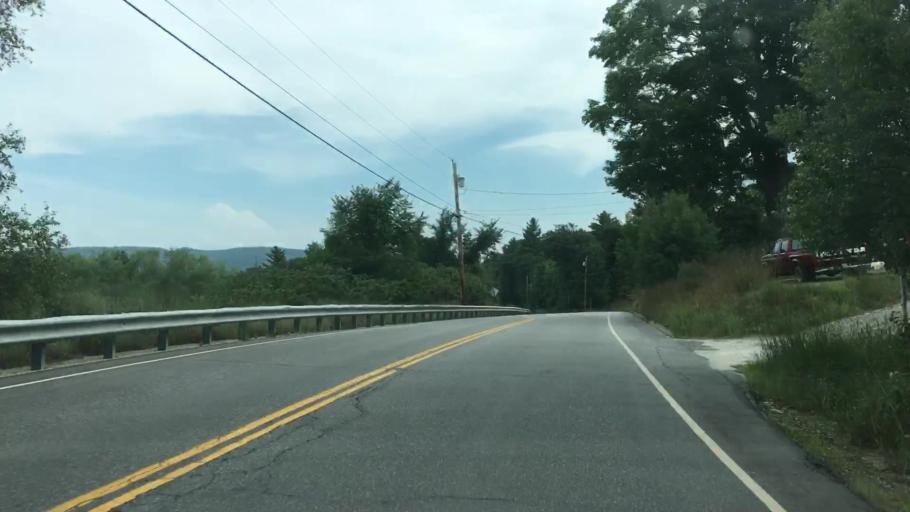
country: US
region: Maine
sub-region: Oxford County
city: Rumford
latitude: 44.5441
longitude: -70.6854
